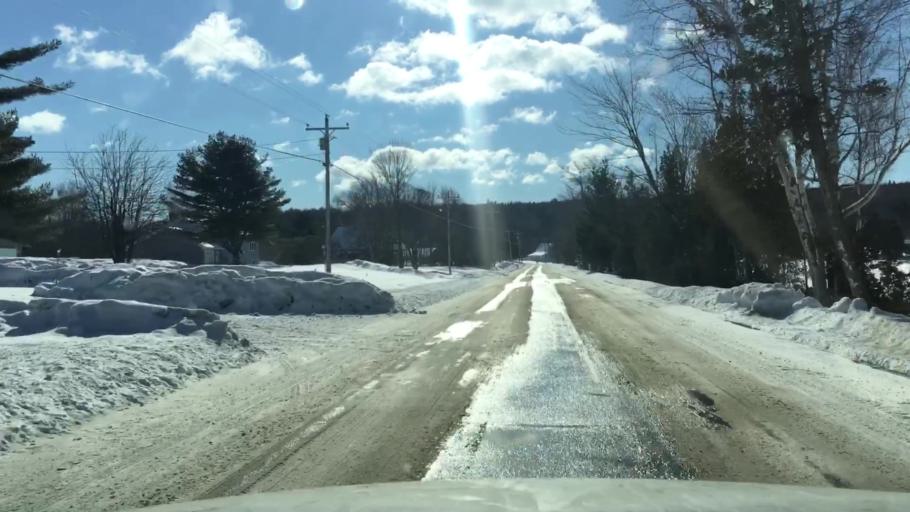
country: US
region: Maine
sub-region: Washington County
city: Calais
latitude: 45.0658
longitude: -67.4727
